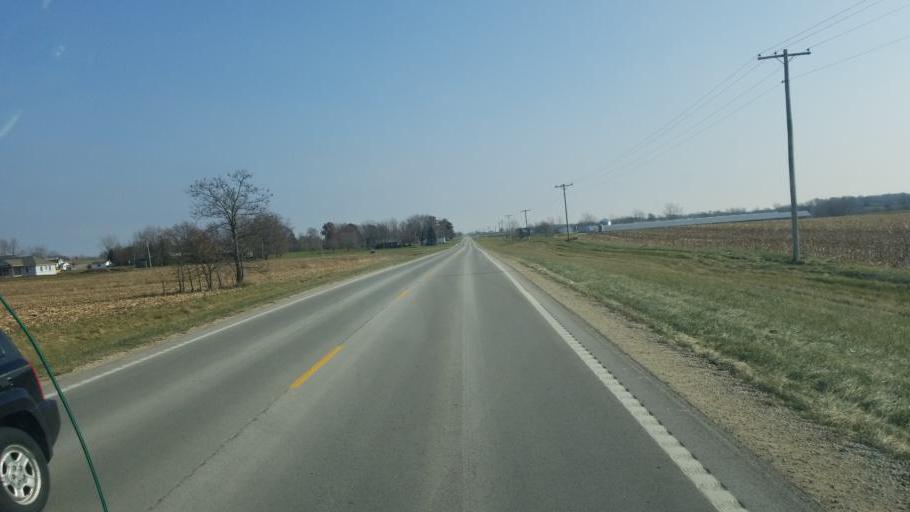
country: US
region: Ohio
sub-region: Mercer County
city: Fort Recovery
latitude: 40.4214
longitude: -84.7421
